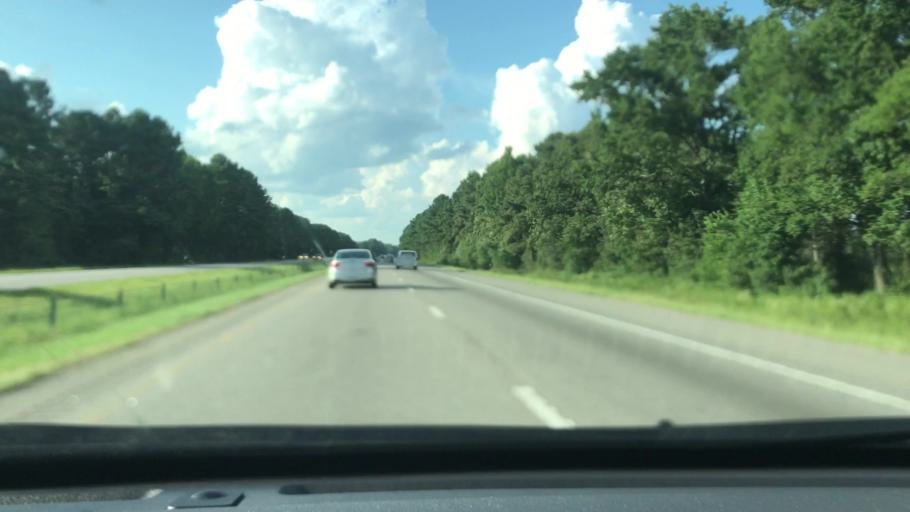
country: US
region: North Carolina
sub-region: Robeson County
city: Saint Pauls
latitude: 34.7552
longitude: -78.9970
